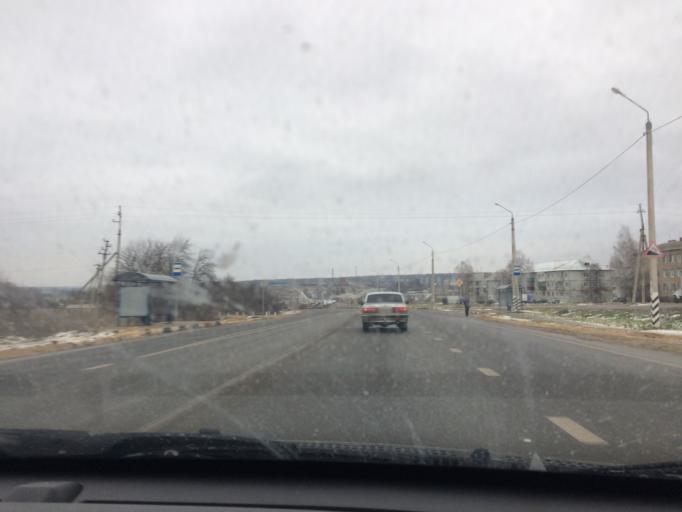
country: RU
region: Tula
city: Gorelki
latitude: 54.2530
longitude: 37.6937
